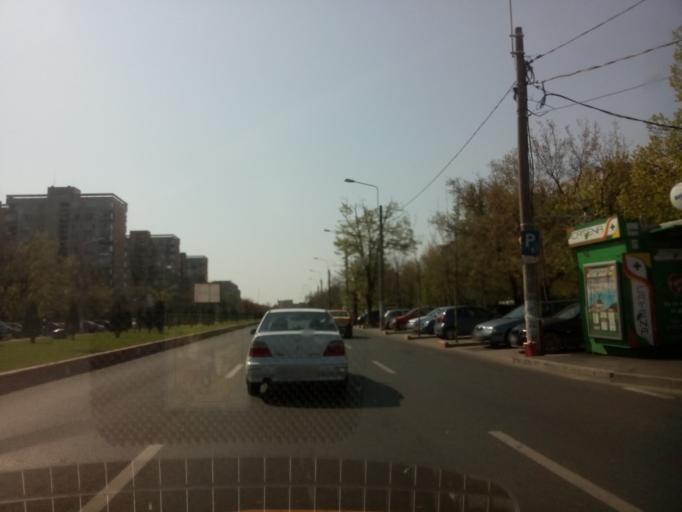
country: RO
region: Ilfov
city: Dobroesti
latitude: 44.4244
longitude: 26.1633
